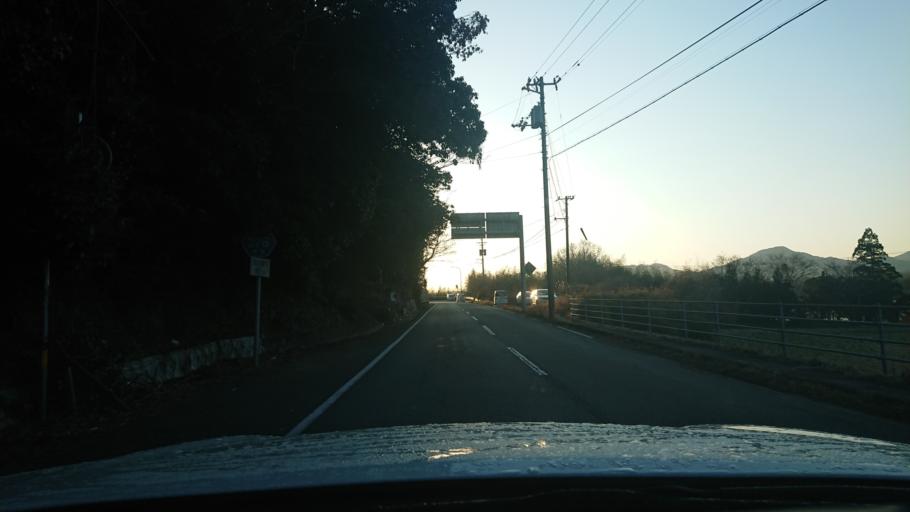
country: JP
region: Tokushima
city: Komatsushimacho
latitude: 33.9437
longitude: 134.5777
